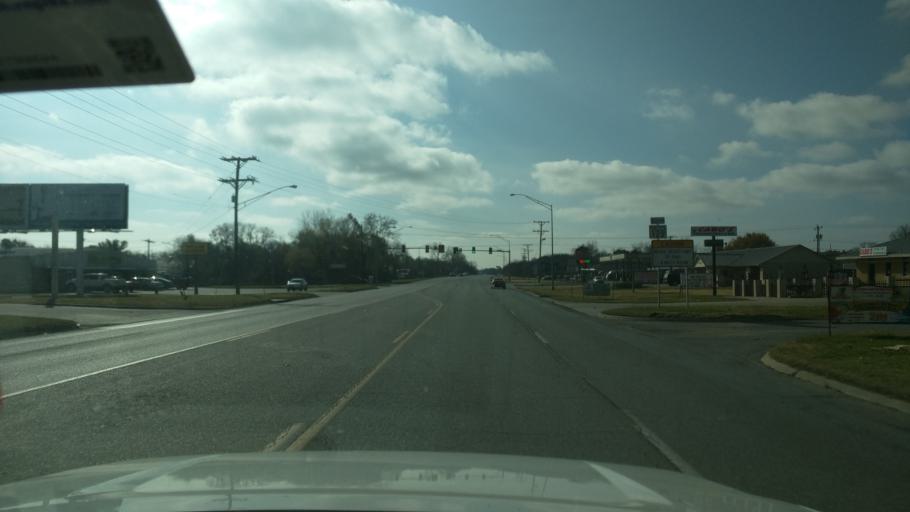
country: US
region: Oklahoma
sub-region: Washington County
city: Dewey
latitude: 36.7873
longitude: -95.9351
